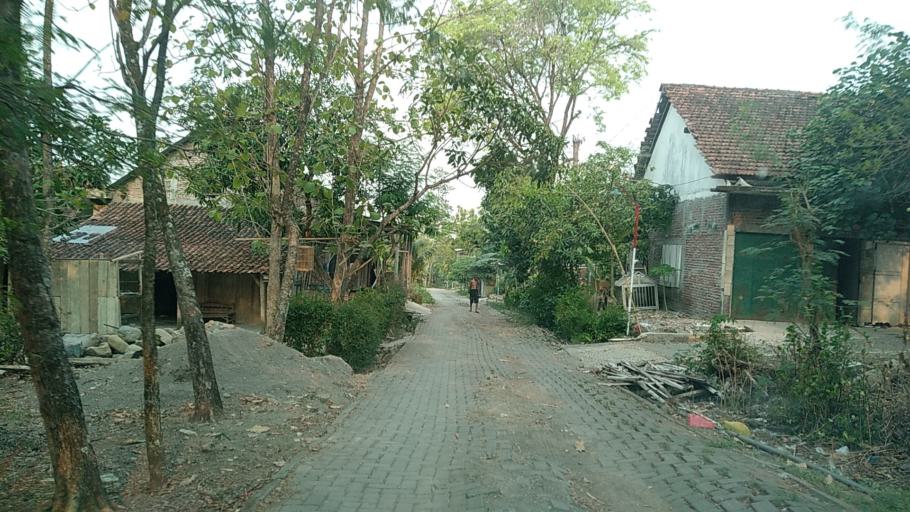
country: ID
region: Central Java
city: Mranggen
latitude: -7.0690
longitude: 110.4847
